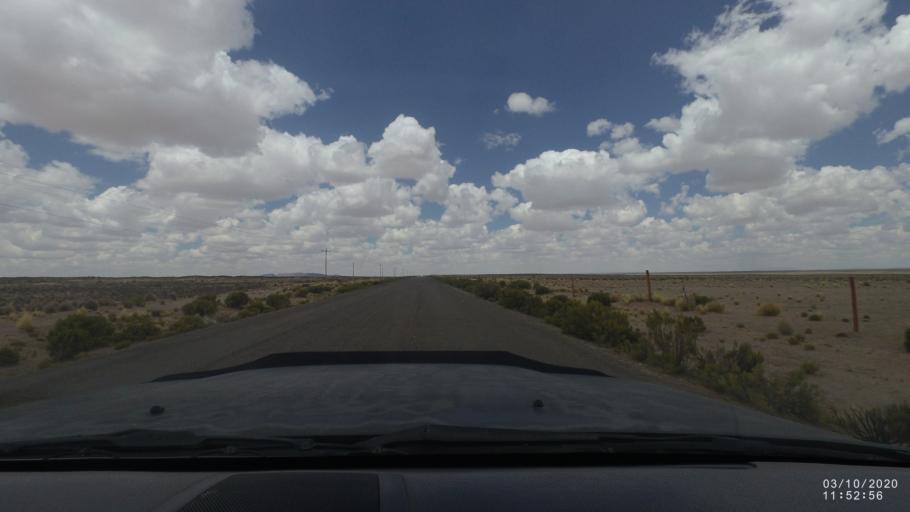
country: BO
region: Oruro
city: Poopo
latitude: -18.4690
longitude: -67.6018
